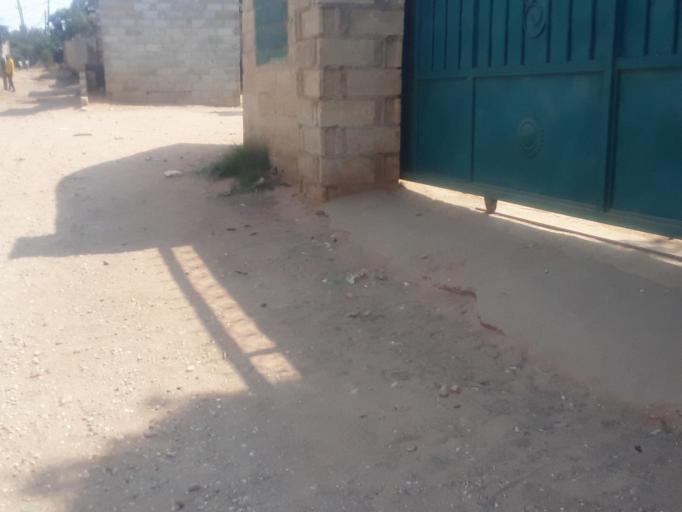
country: ZM
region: Lusaka
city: Lusaka
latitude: -15.3531
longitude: 28.2930
